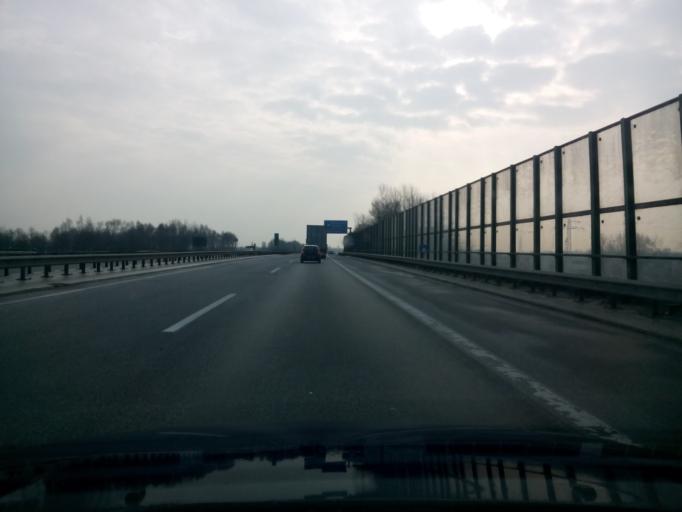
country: DE
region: Lower Saxony
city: Loxstedt
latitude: 53.4996
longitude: 8.6276
